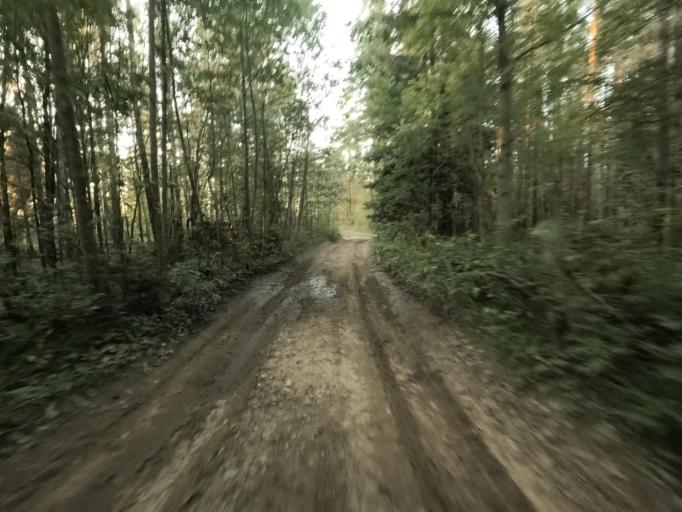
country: RU
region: Leningrad
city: Otradnoye
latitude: 59.8397
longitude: 30.8038
